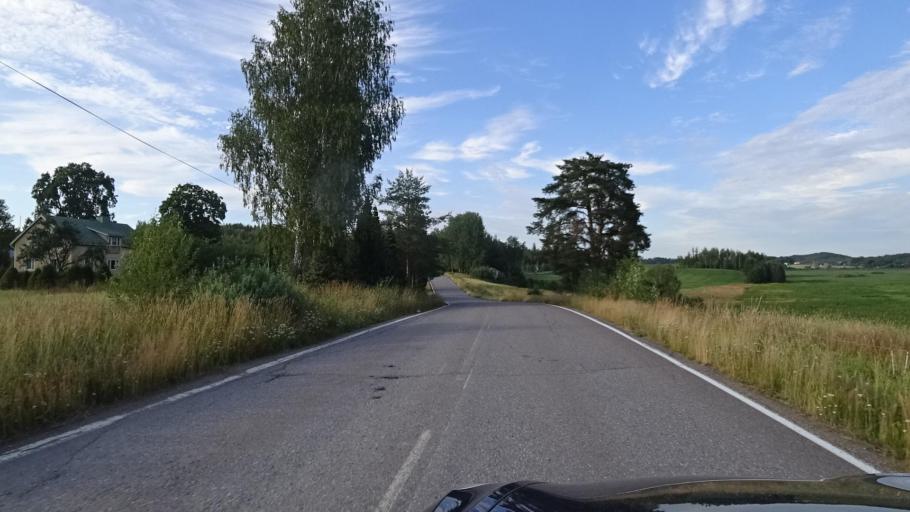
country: FI
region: Uusimaa
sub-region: Helsinki
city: Saukkola
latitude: 60.3927
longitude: 24.0276
